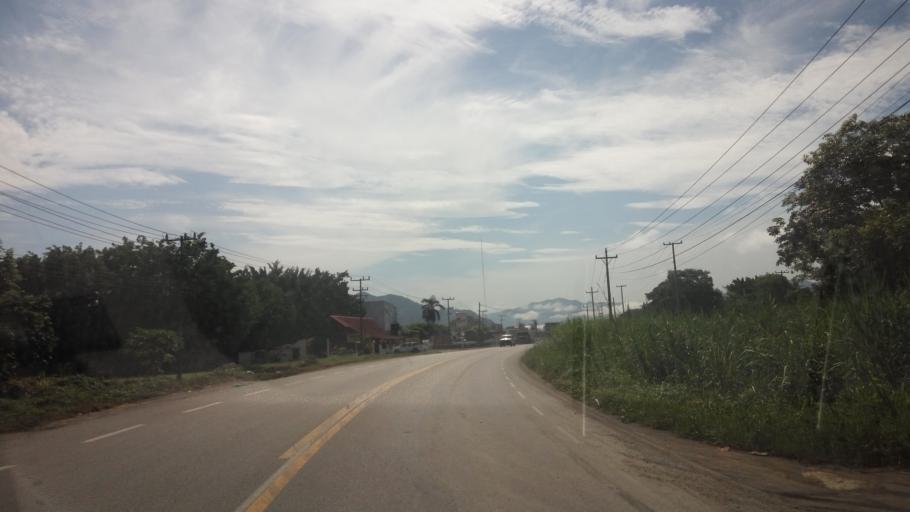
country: MX
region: Tabasco
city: Teapa
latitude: 17.5808
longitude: -92.9646
